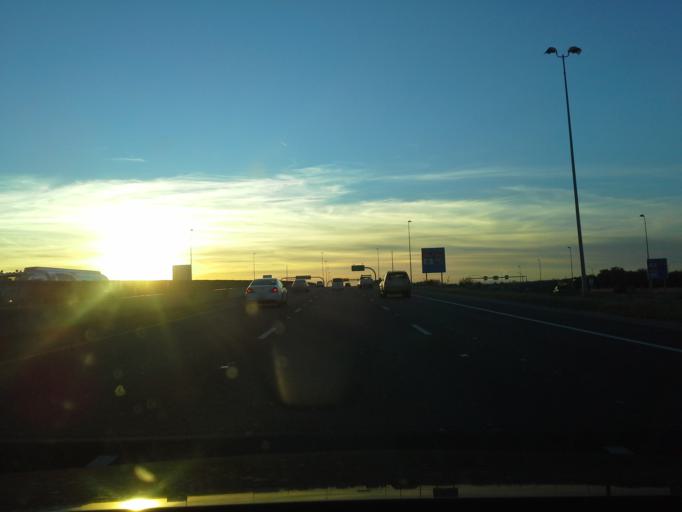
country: US
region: Arizona
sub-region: Pinal County
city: Apache Junction
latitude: 33.3867
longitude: -111.6115
